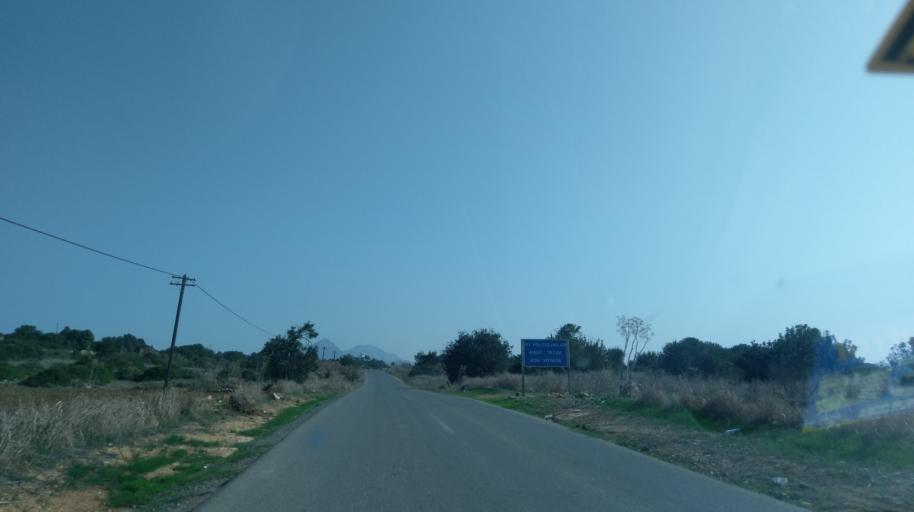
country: CY
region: Lefkosia
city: Morfou
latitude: 35.3411
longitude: 33.0177
